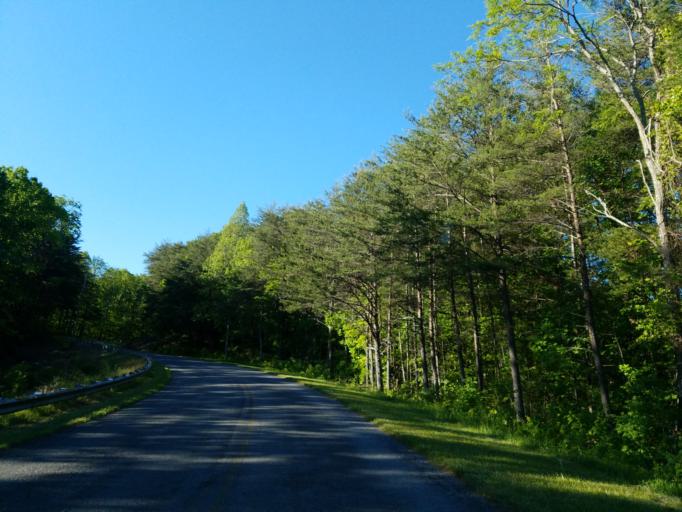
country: US
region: Georgia
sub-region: Fannin County
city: Blue Ridge
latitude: 34.7196
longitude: -84.2886
